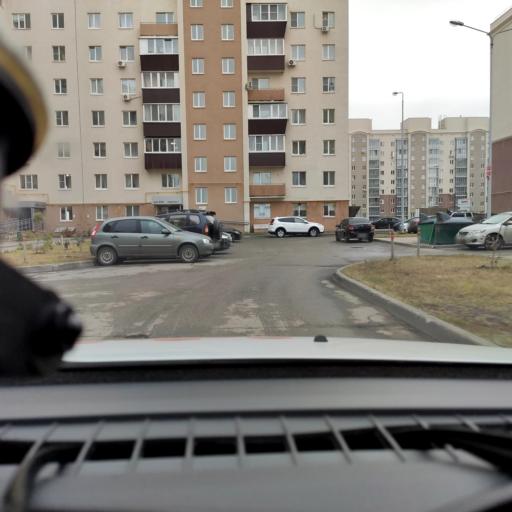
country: RU
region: Samara
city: Samara
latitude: 53.1146
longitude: 50.1476
